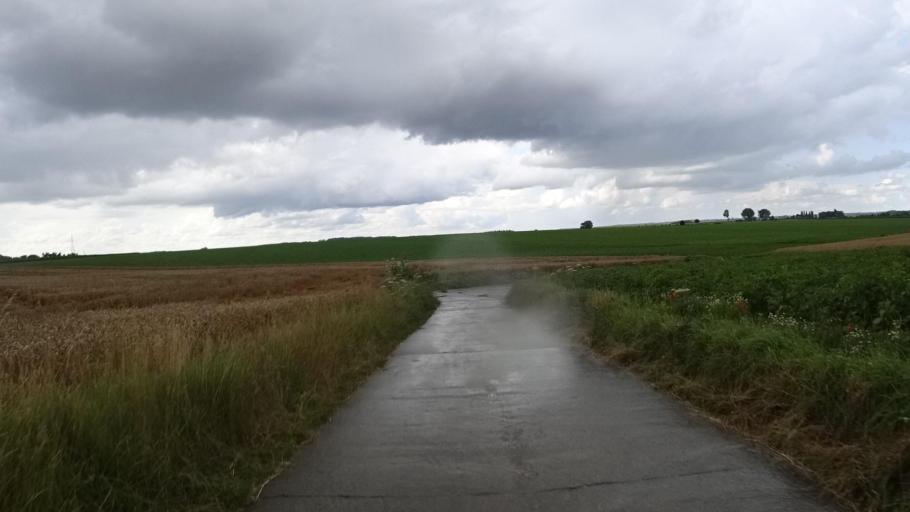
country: BE
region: Wallonia
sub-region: Province du Brabant Wallon
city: Chastre
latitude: 50.5920
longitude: 4.6225
